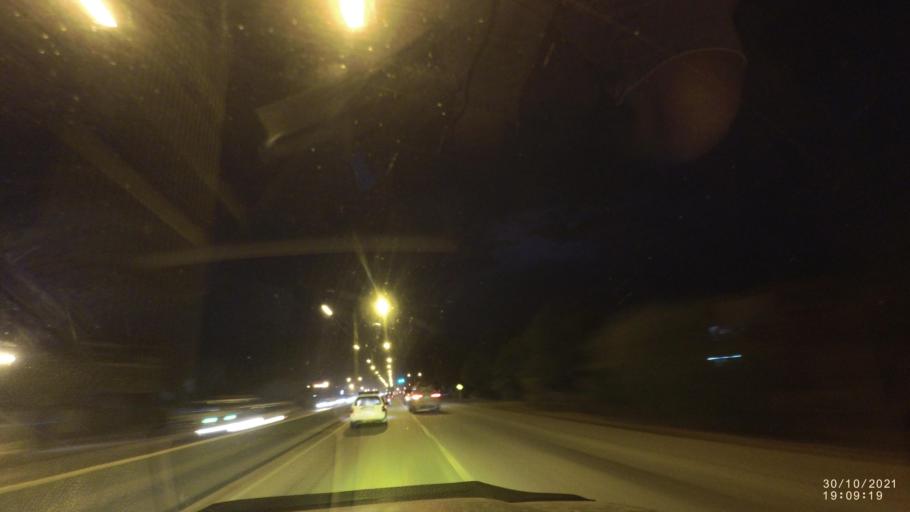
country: BO
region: Cochabamba
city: Sipe Sipe
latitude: -17.4215
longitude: -66.3322
